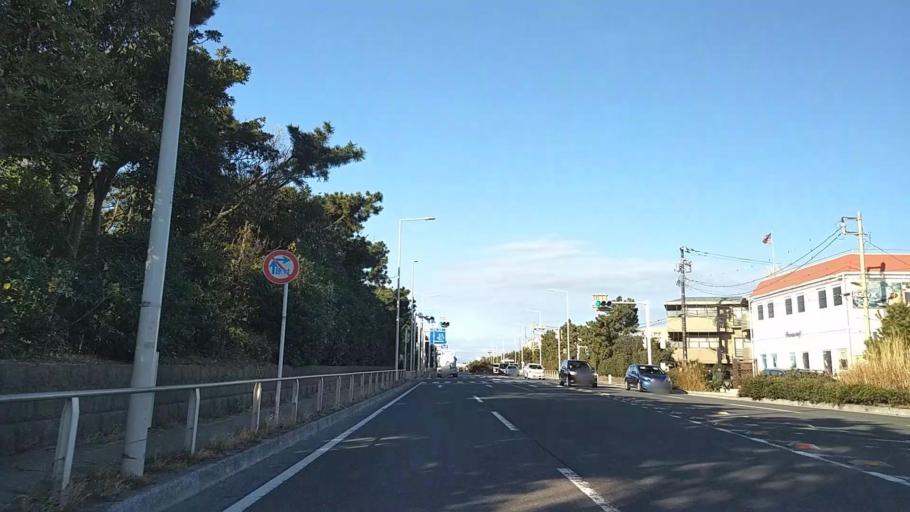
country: JP
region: Kanagawa
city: Fujisawa
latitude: 35.3170
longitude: 139.4648
